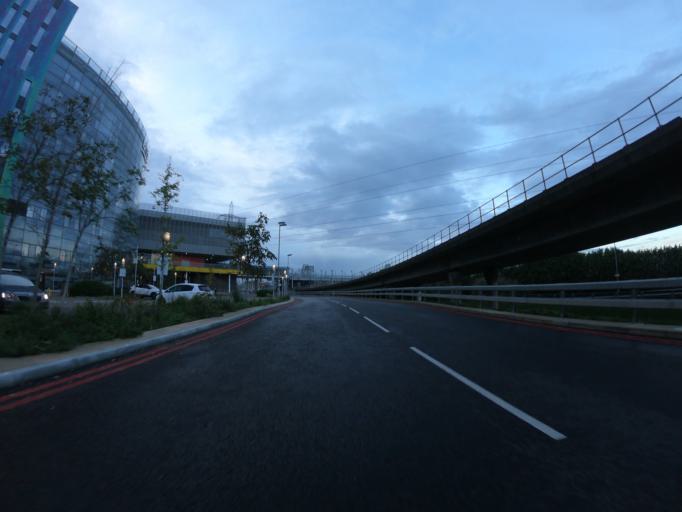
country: GB
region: England
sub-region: Greater London
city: East Ham
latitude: 51.5087
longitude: 0.0358
